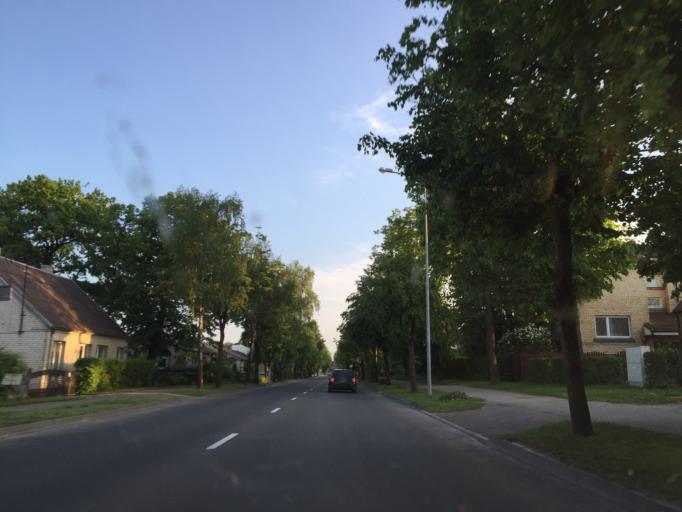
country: LT
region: Siauliu apskritis
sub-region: Siauliai
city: Siauliai
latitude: 55.9454
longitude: 23.3181
